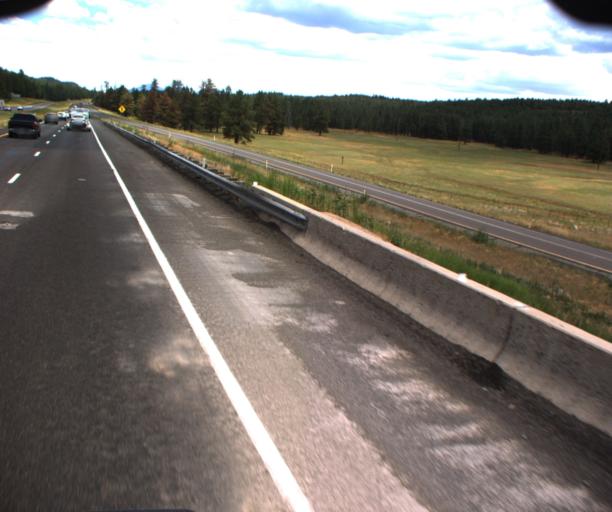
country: US
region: Arizona
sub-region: Coconino County
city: Mountainaire
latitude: 34.9818
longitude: -111.6860
